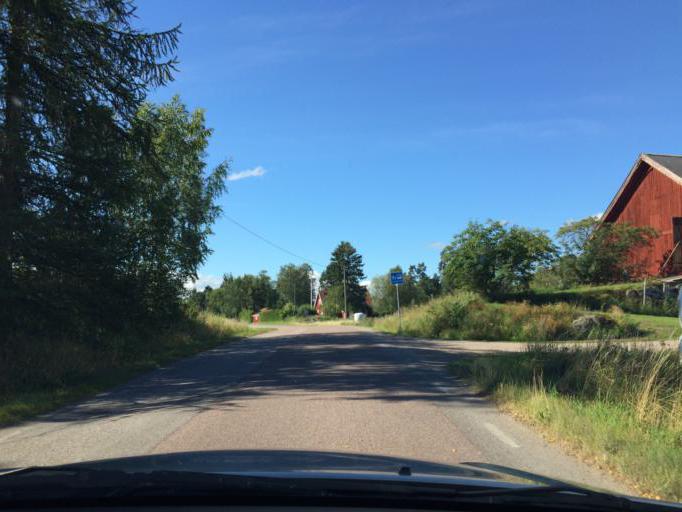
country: SE
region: Soedermanland
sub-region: Eskilstuna Kommun
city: Torshalla
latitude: 59.5331
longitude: 16.4458
